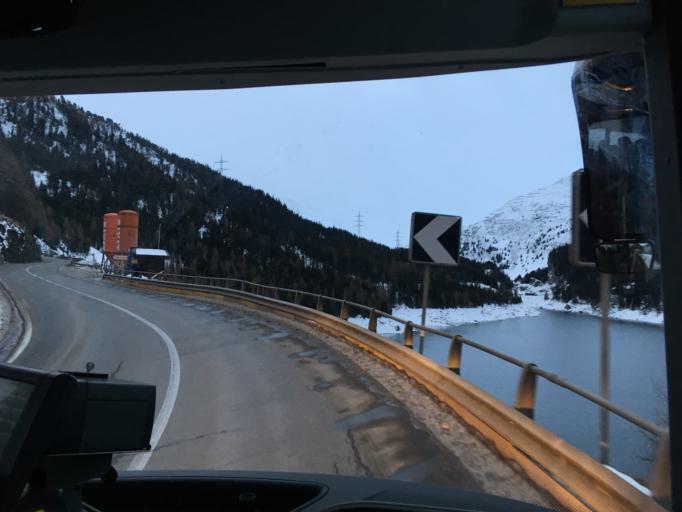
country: CH
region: Grisons
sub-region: Maloja District
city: Silvaplana
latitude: 46.4976
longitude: 9.6418
